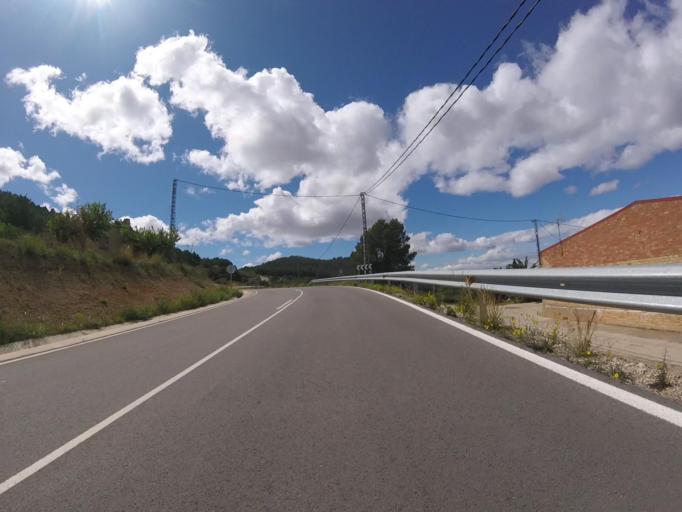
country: ES
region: Valencia
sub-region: Provincia de Castello
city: Culla
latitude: 40.2794
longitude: -0.1121
